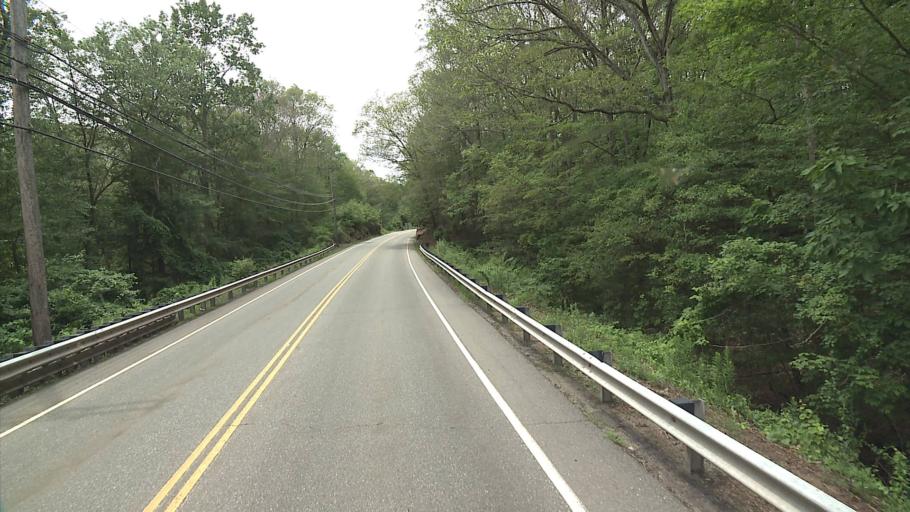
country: US
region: Connecticut
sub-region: New Haven County
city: Guilford
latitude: 41.3585
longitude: -72.6413
